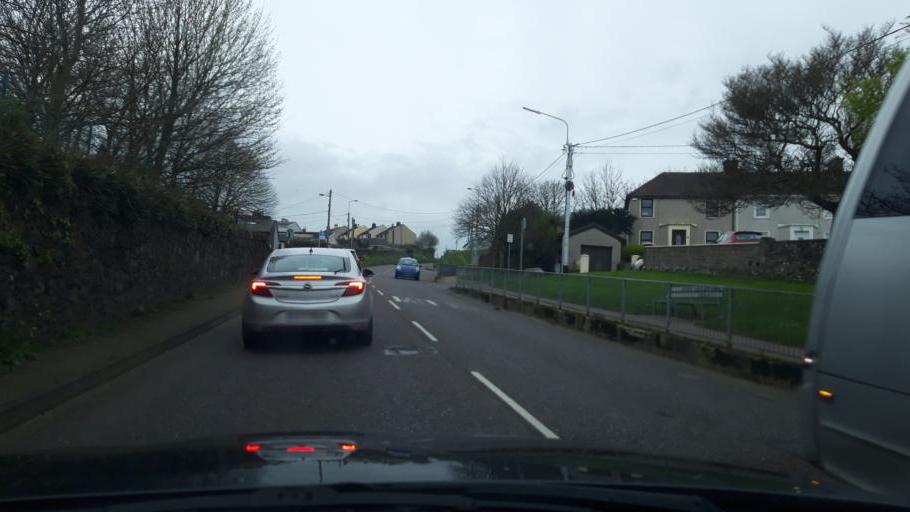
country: IE
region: Munster
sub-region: County Cork
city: Cork
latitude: 51.9172
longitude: -8.4692
